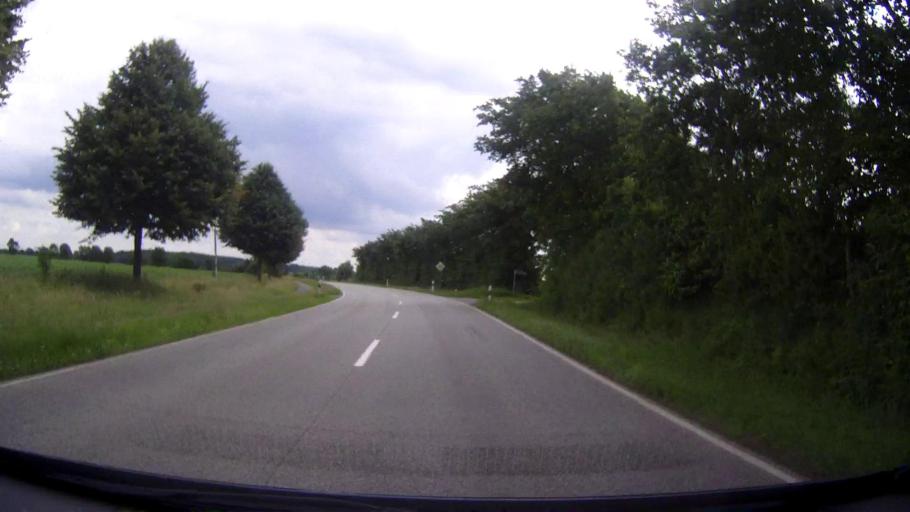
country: DE
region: Schleswig-Holstein
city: Seefeld
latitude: 54.0972
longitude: 9.4679
